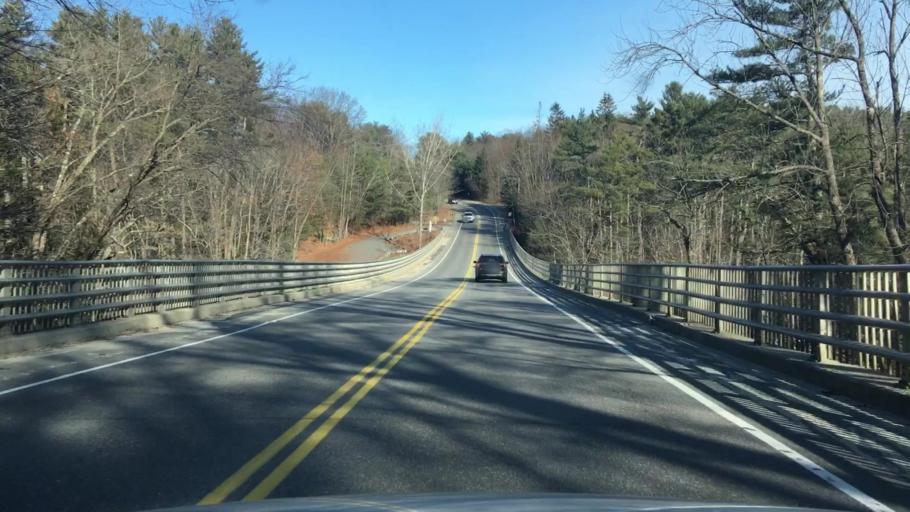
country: US
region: Maine
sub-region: Cumberland County
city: Falmouth
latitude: 43.7165
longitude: -70.2648
